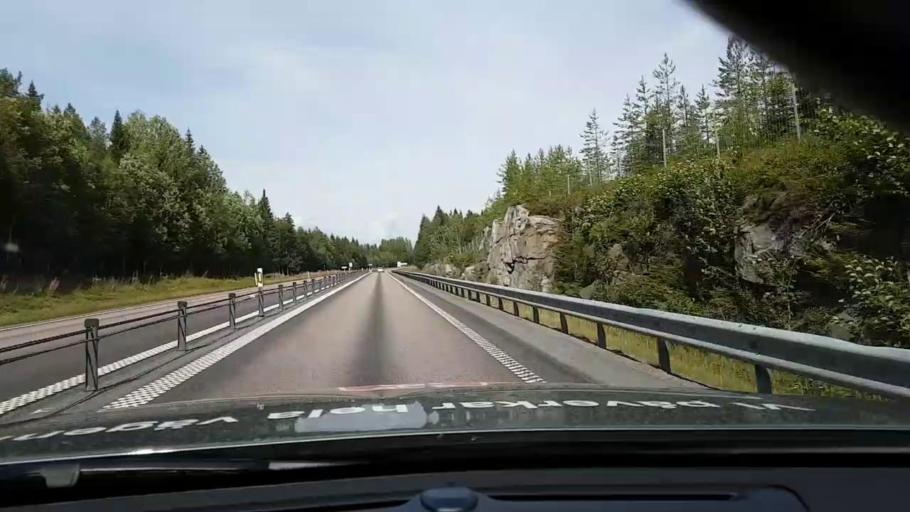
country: SE
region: Vaesternorrland
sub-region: OErnskoeldsviks Kommun
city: Husum
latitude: 63.4344
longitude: 19.2108
